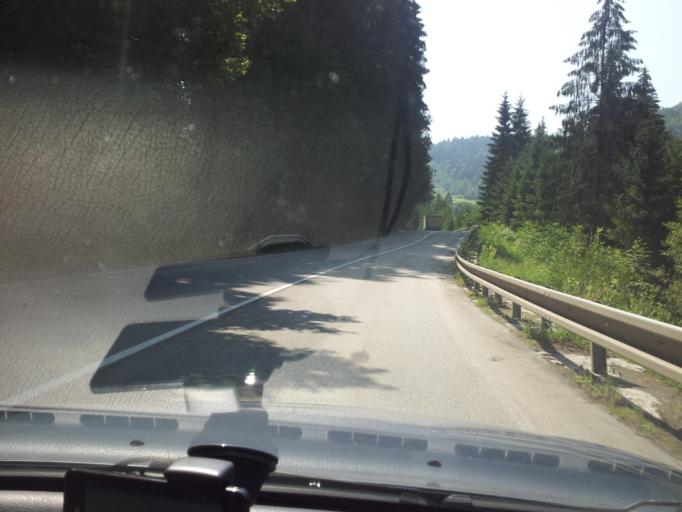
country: SK
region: Zilinsky
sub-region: Okres Dolny Kubin
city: Dolny Kubin
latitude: 49.2735
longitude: 19.3505
